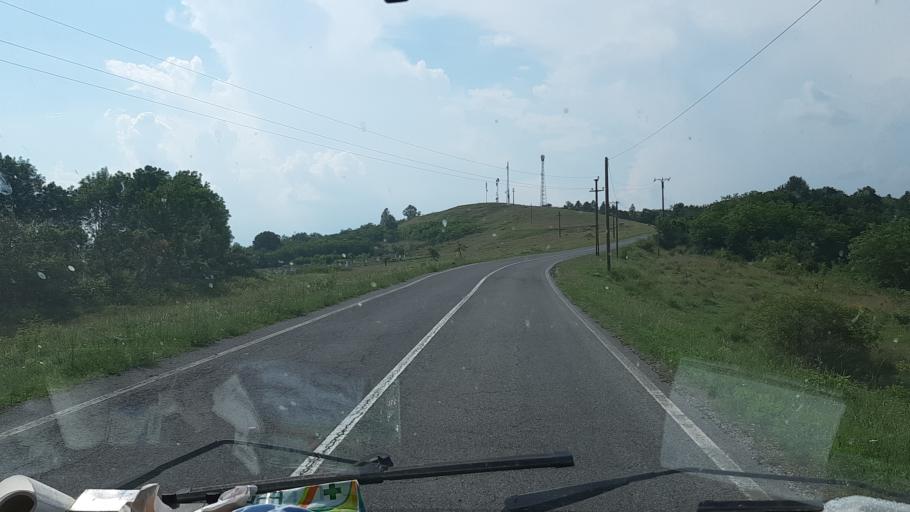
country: RO
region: Caras-Severin
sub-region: Comuna Farliug
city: Farliug
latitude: 45.5151
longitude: 21.8770
